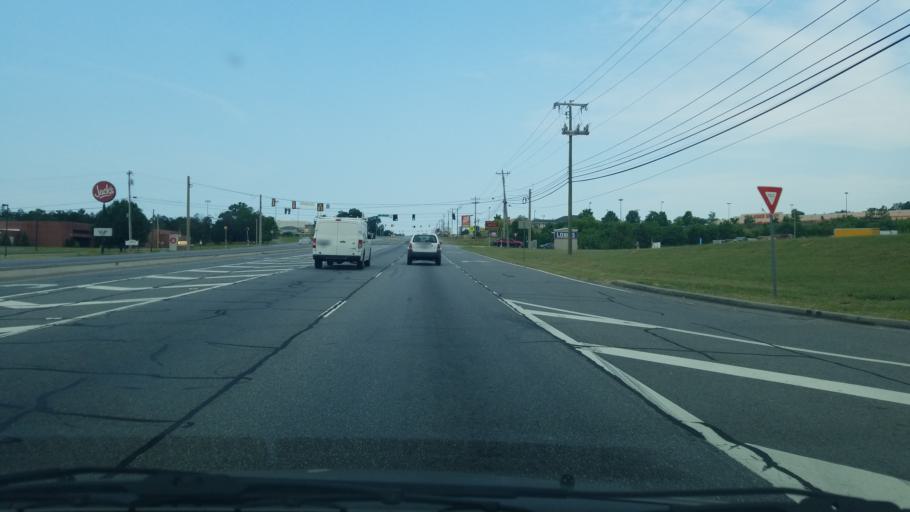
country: US
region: Georgia
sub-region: Catoosa County
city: Fort Oglethorpe
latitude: 34.9448
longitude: -85.2271
